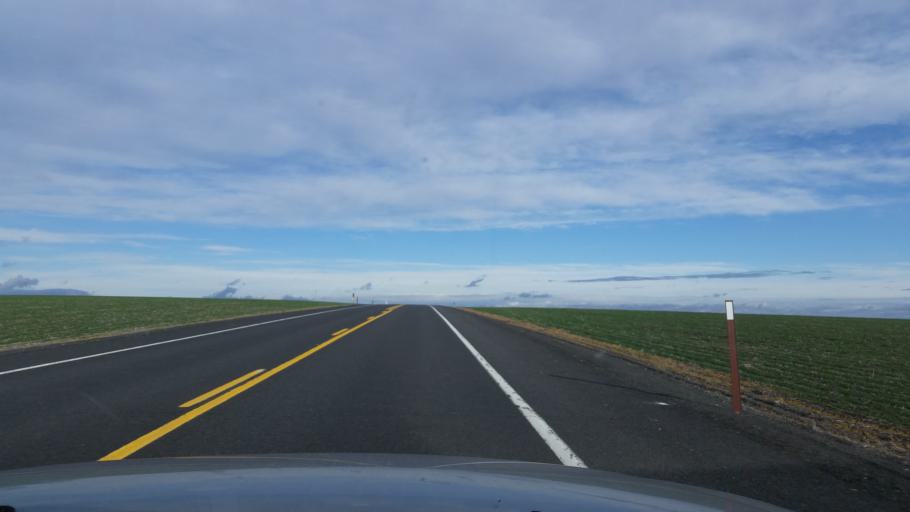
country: US
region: Washington
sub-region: Adams County
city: Ritzville
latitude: 47.4050
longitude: -118.3848
